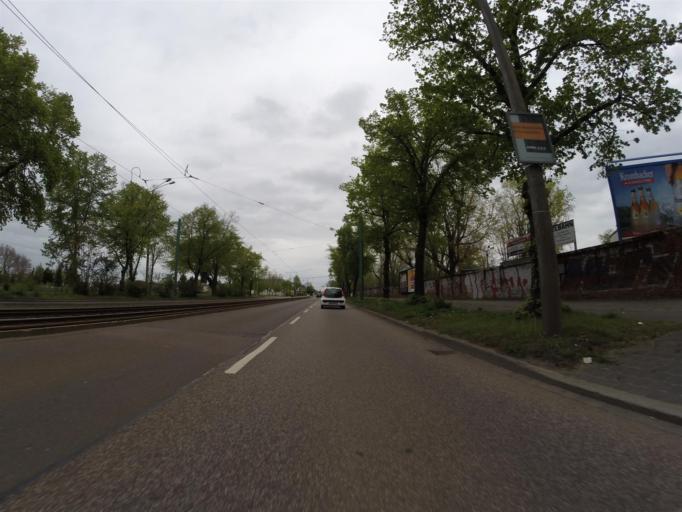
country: DE
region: Saxony-Anhalt
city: Schkopau
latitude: 51.4331
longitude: 11.9842
